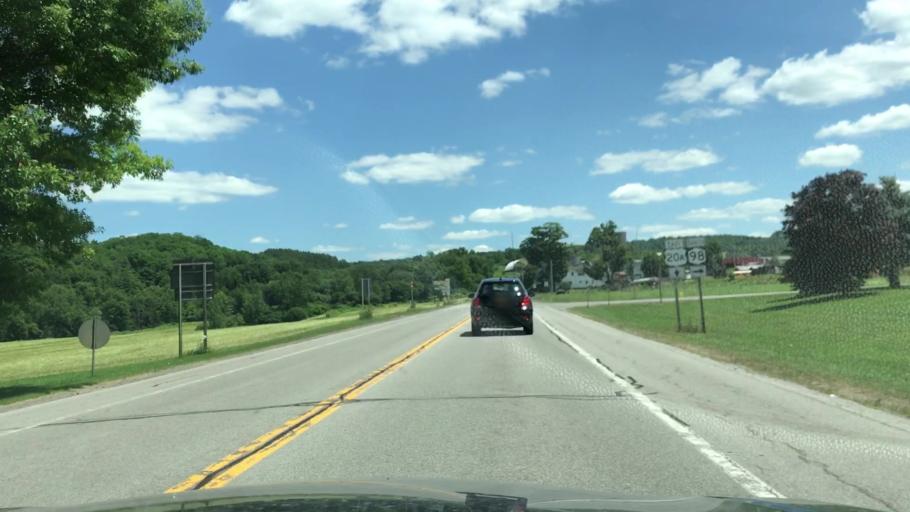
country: US
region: New York
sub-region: Wyoming County
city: Attica
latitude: 42.7569
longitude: -78.3058
